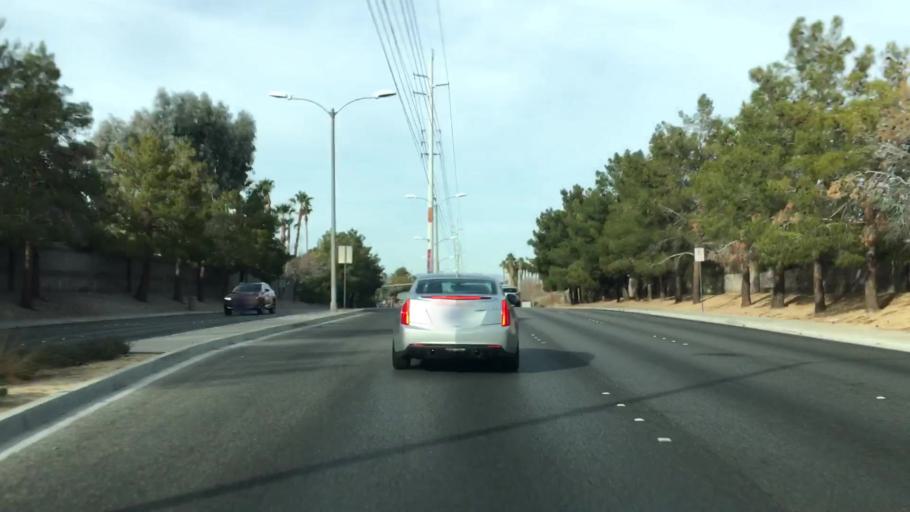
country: US
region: Nevada
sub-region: Clark County
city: Whitney
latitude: 36.0469
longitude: -115.0823
